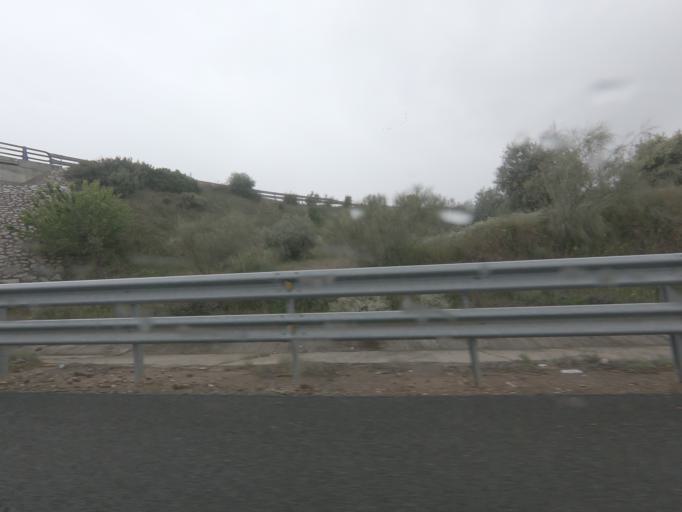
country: ES
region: Extremadura
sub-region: Provincia de Caceres
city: Plasencia
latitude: 40.0347
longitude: -6.1221
